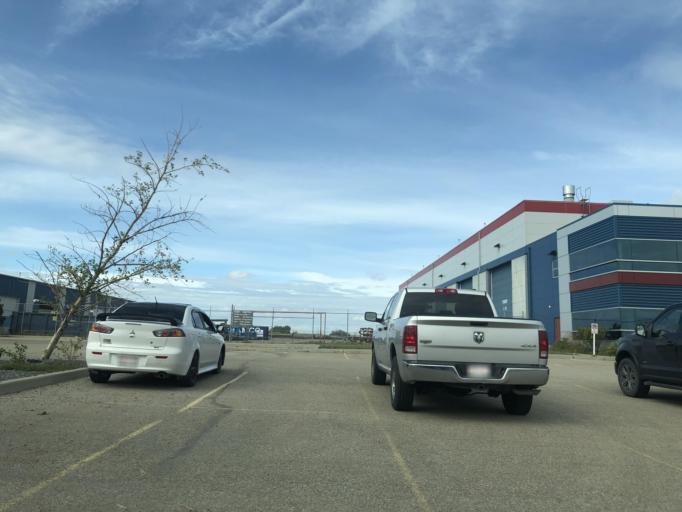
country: CA
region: Alberta
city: Chestermere
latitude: 50.9706
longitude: -113.9048
